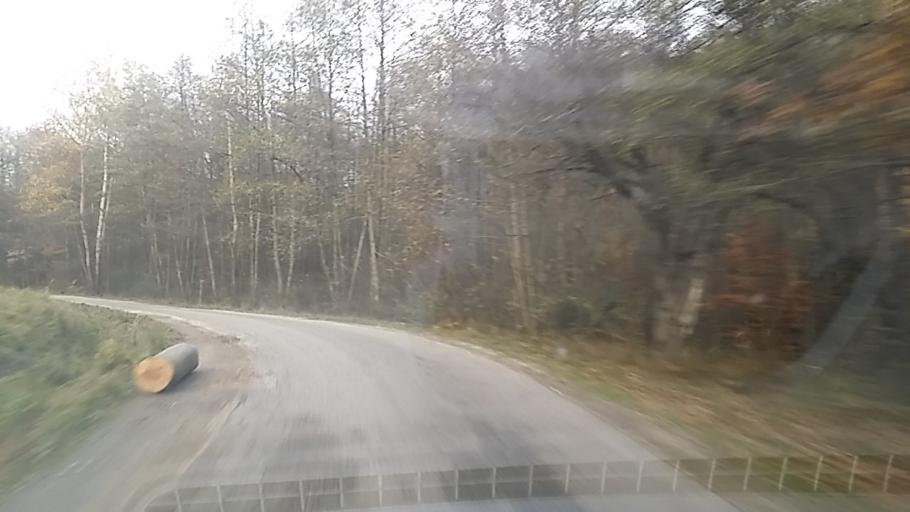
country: HU
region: Borsod-Abauj-Zemplen
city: Tolcsva
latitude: 48.4377
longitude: 21.4608
